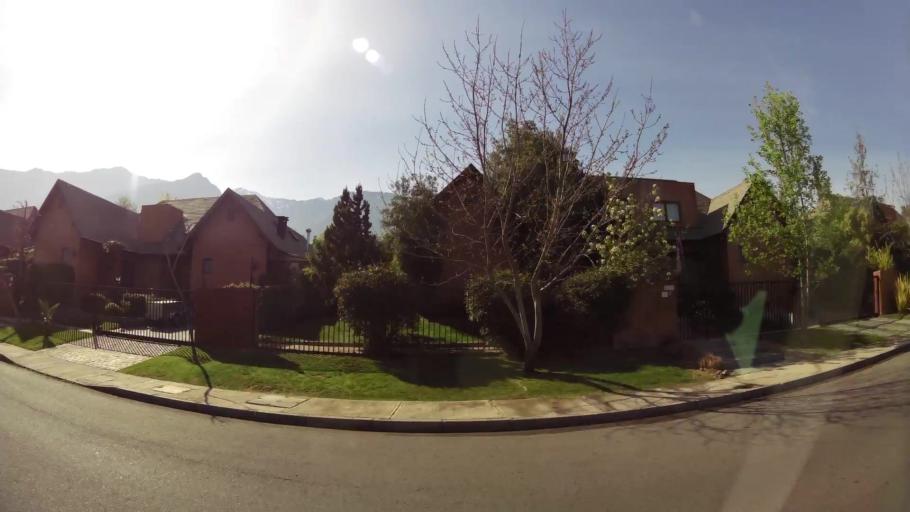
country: CL
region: Santiago Metropolitan
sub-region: Provincia de Santiago
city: Villa Presidente Frei, Nunoa, Santiago, Chile
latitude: -33.4990
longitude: -70.5266
